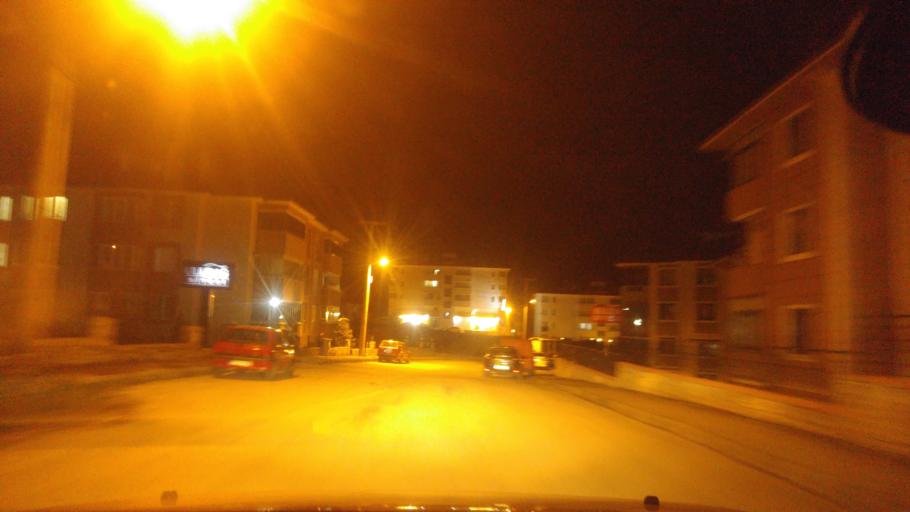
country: TR
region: Karabuk
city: Safranbolu
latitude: 41.2647
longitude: 32.6766
